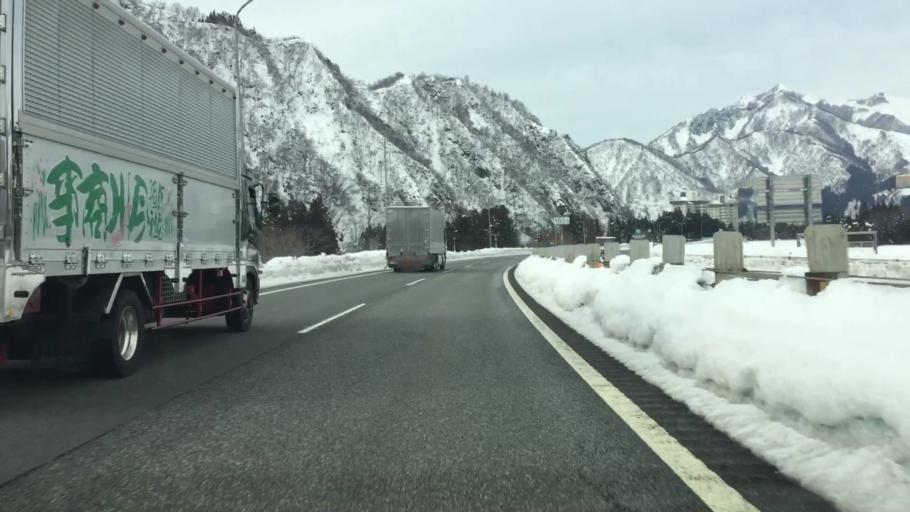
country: JP
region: Niigata
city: Shiozawa
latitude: 36.9102
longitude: 138.8404
